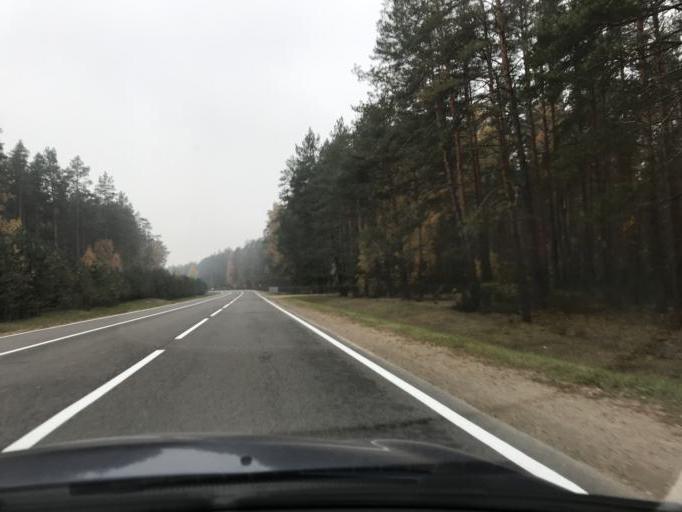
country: LT
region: Alytaus apskritis
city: Druskininkai
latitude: 53.9202
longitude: 23.9272
